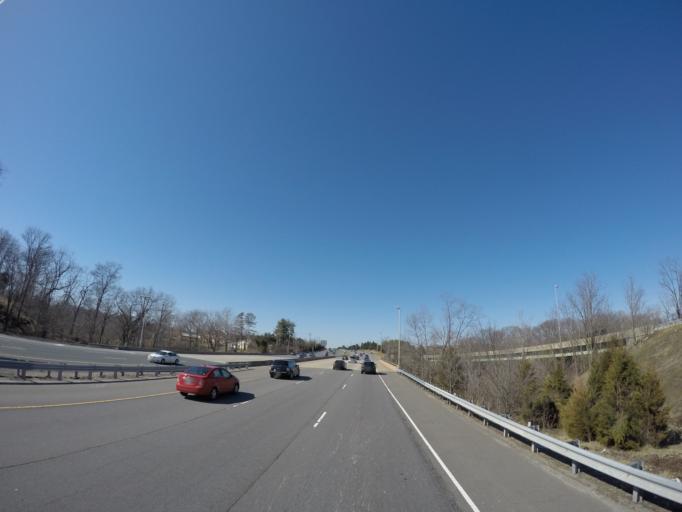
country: US
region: Virginia
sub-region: Loudoun County
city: University Center
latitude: 39.0465
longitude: -77.4317
